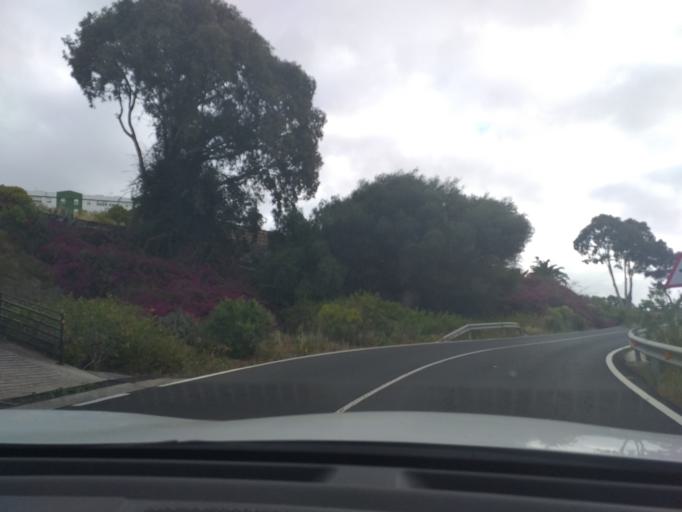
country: ES
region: Canary Islands
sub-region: Provincia de Las Palmas
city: Arucas
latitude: 28.1076
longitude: -15.5046
